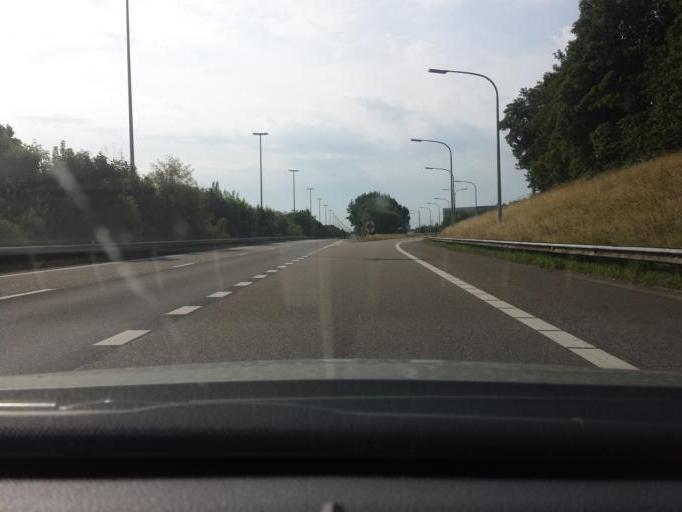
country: BE
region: Flanders
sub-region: Provincie Limburg
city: Tongeren
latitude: 50.7928
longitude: 5.5312
